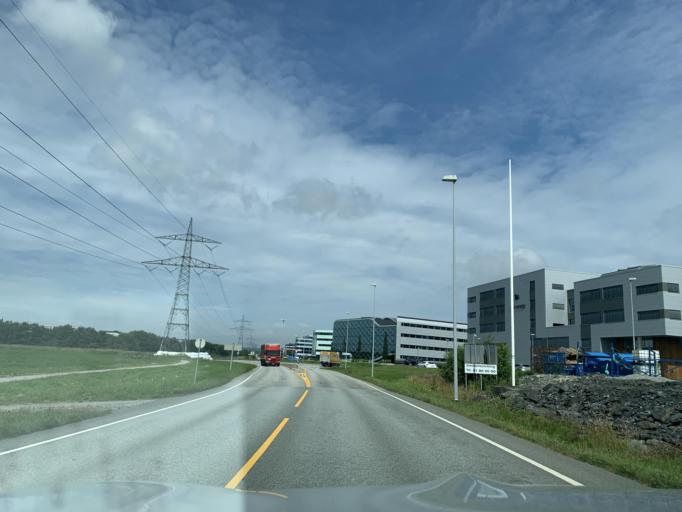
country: NO
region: Rogaland
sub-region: Sola
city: Sola
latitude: 58.8856
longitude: 5.6957
